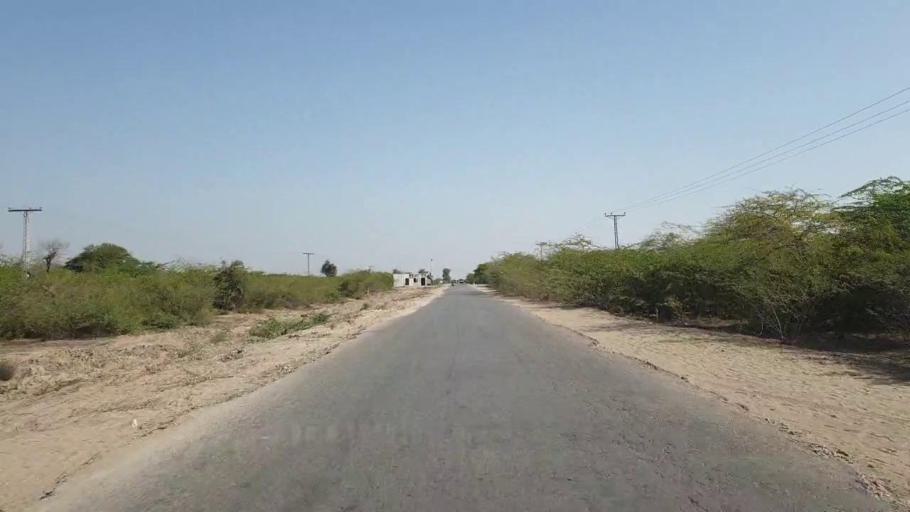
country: PK
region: Sindh
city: Chor
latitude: 25.4594
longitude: 69.7625
